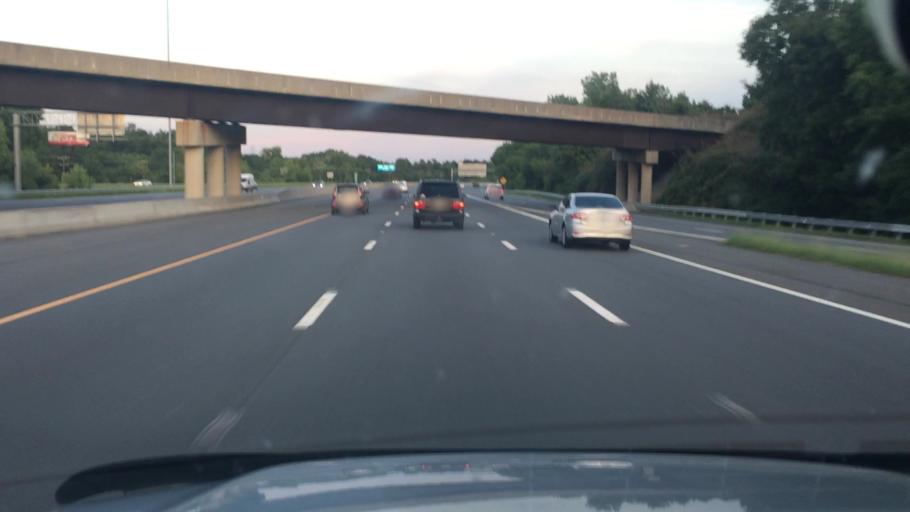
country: US
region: North Carolina
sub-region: Mecklenburg County
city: Pineville
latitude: 35.1234
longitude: -80.9132
